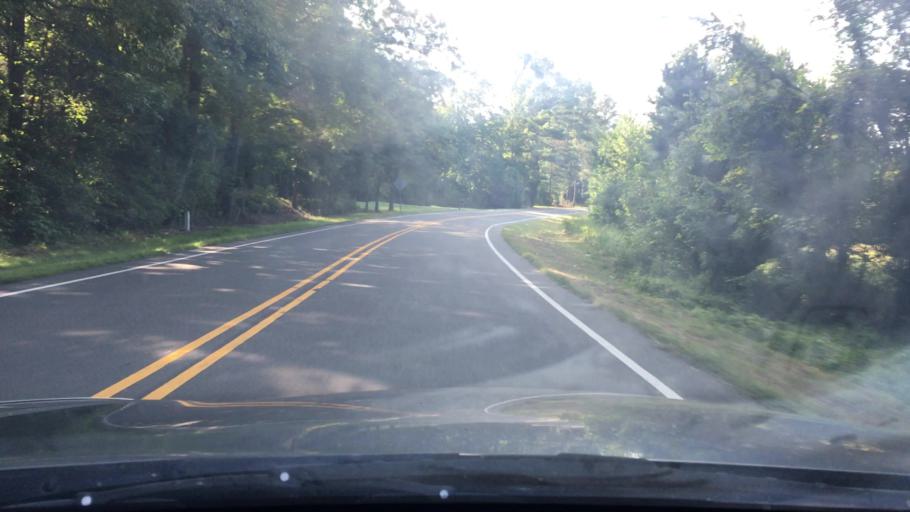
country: US
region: North Carolina
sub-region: Alamance County
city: Green Level
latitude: 36.2538
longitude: -79.3324
